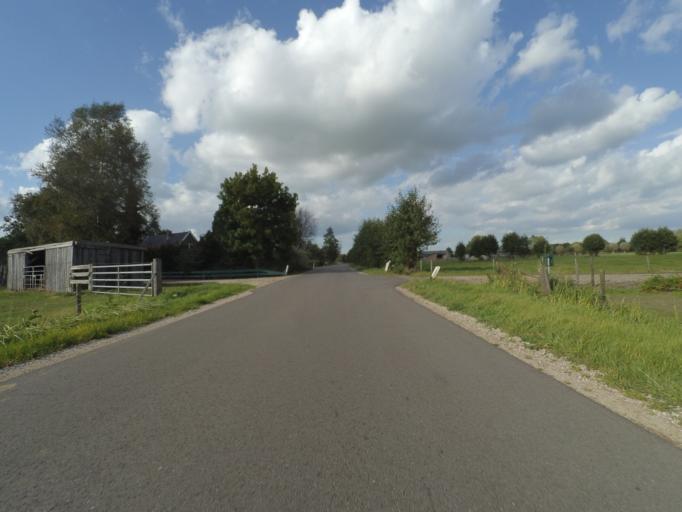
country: NL
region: Gelderland
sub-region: Gemeente Ede
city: Lunteren
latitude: 52.0525
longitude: 5.6127
